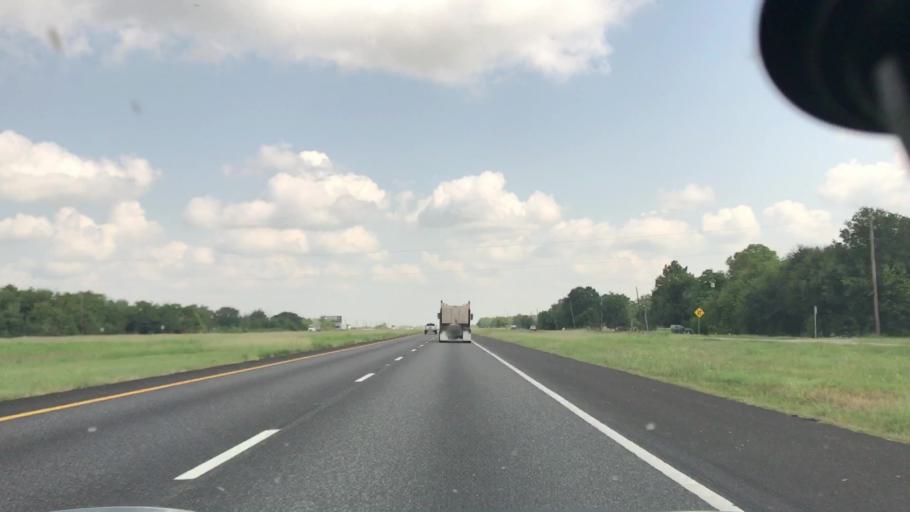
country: US
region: Texas
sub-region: Brazoria County
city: Rosharon
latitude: 29.3958
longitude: -95.4262
